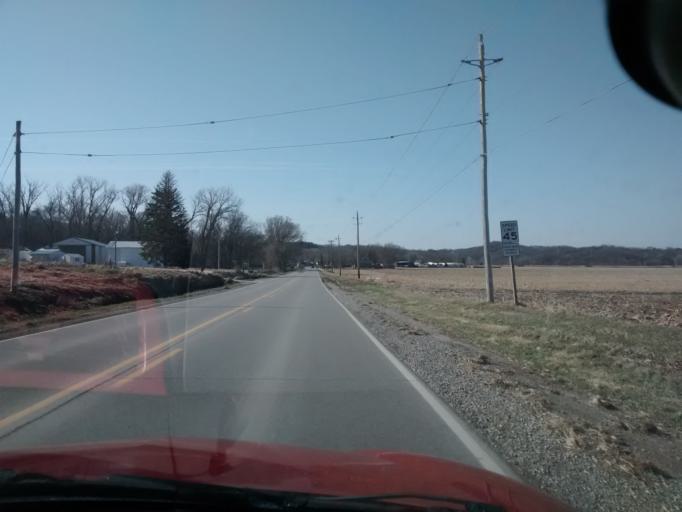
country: US
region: Iowa
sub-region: Pottawattamie County
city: Carter Lake
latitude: 41.3734
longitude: -95.8572
